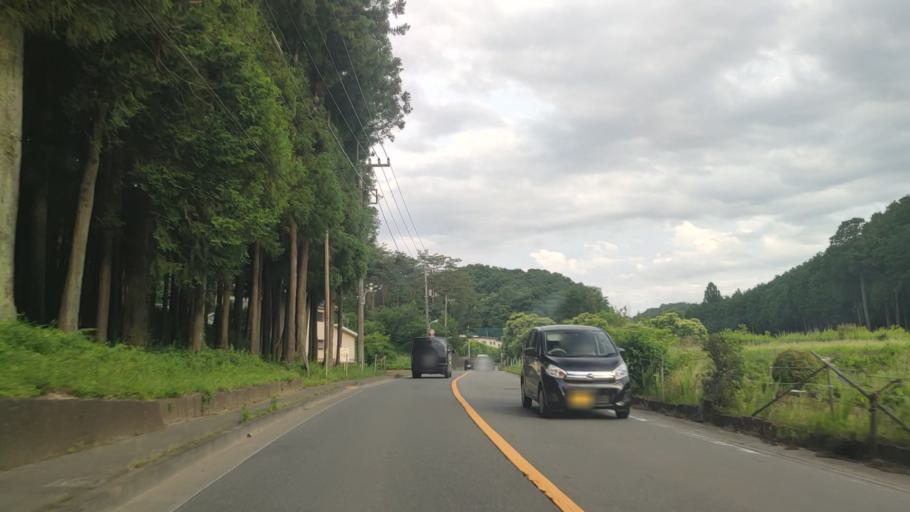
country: JP
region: Saitama
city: Hanno
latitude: 35.8176
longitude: 139.2962
